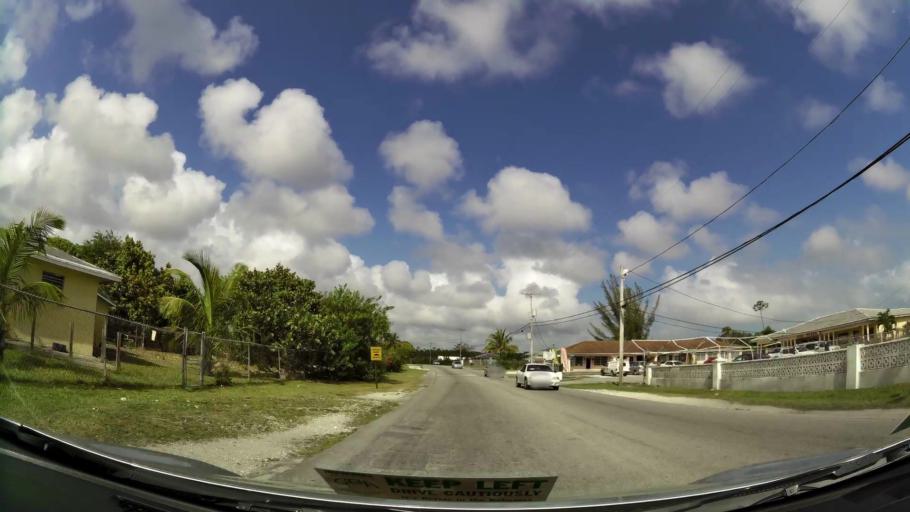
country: BS
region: Freeport
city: Lucaya
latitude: 26.5308
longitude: -78.6753
